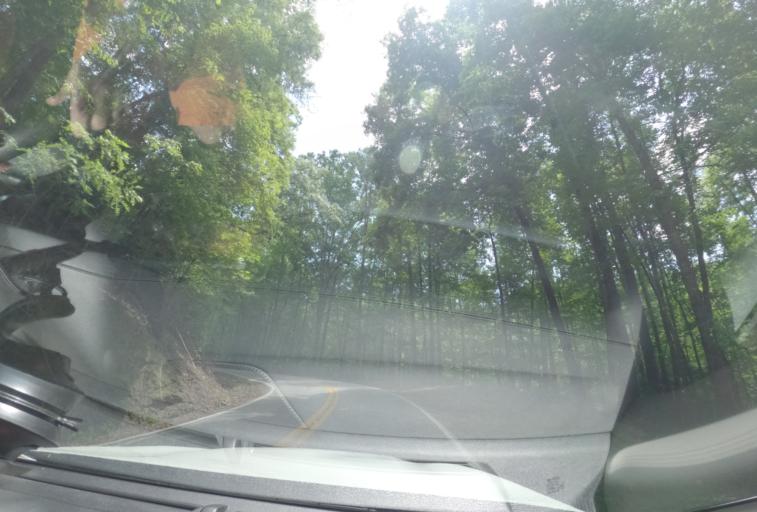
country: US
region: South Carolina
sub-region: Pickens County
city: Pickens
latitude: 35.0019
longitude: -82.8204
